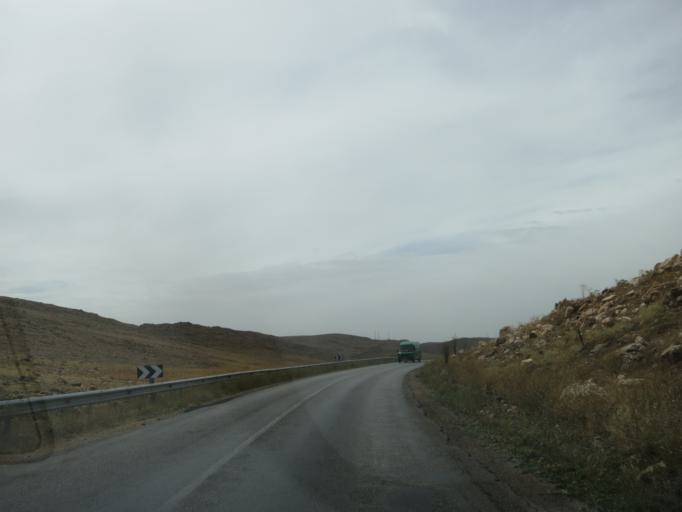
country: MA
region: Meknes-Tafilalet
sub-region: Khenifra
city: Itzer
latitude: 33.1795
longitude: -5.0605
